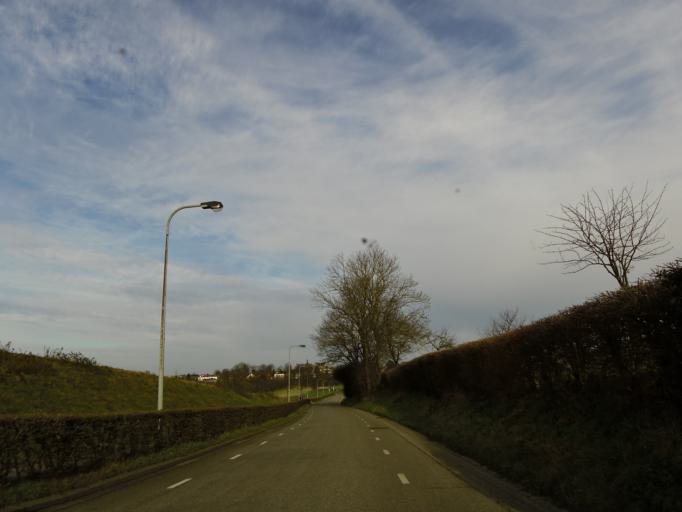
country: NL
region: Limburg
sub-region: Gemeente Voerendaal
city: Ubachsberg
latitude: 50.8468
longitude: 5.9473
